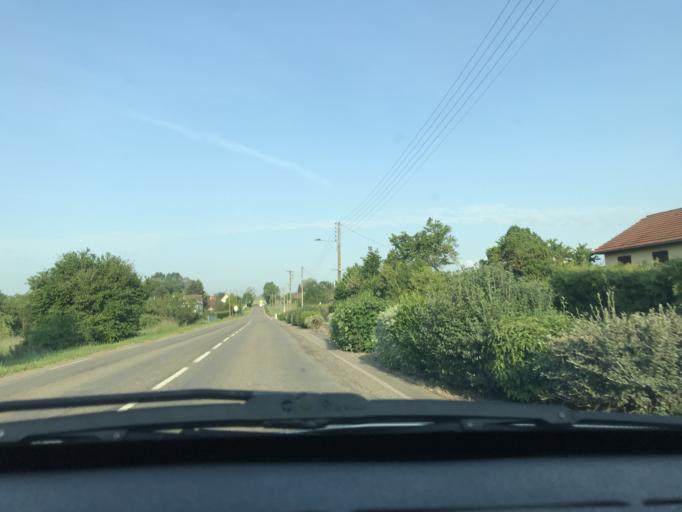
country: FR
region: Lorraine
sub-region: Departement de la Moselle
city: Vic-sur-Seille
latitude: 48.7783
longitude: 6.5591
